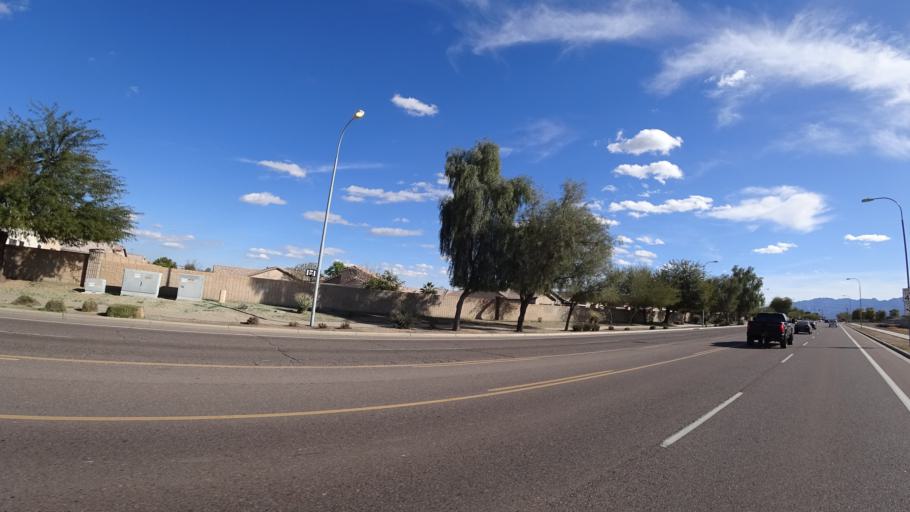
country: US
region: Arizona
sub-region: Maricopa County
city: Tolleson
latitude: 33.4149
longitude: -112.2214
